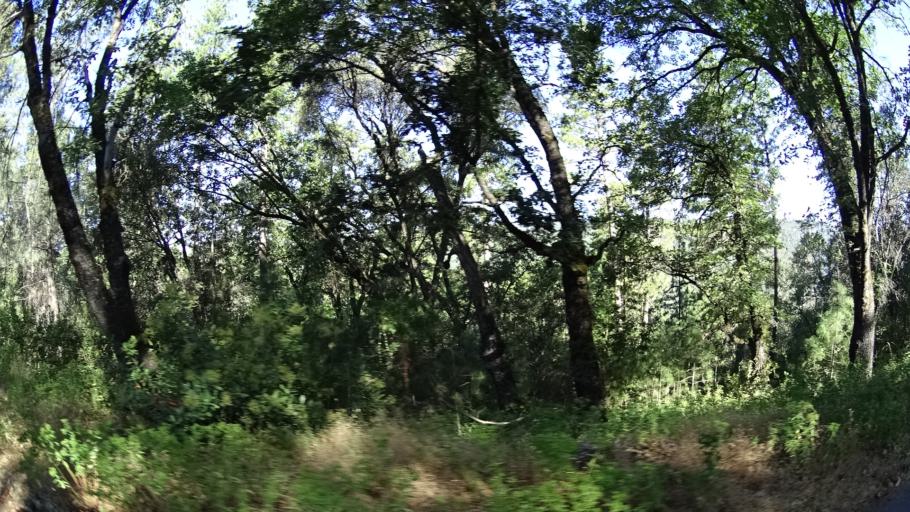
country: US
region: California
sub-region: Amador County
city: Pioneer
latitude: 38.3999
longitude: -120.5682
